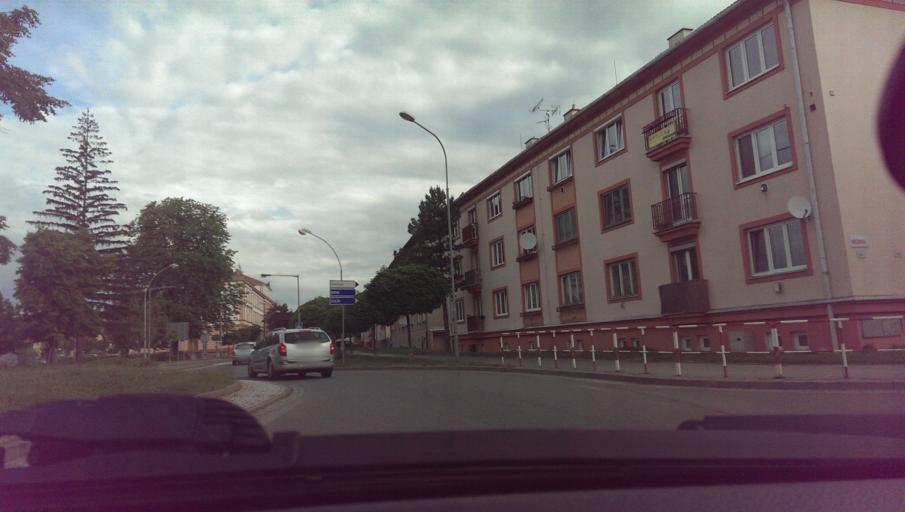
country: CZ
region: Zlin
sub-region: Okres Kromeriz
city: Kromeriz
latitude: 49.2922
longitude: 17.3918
